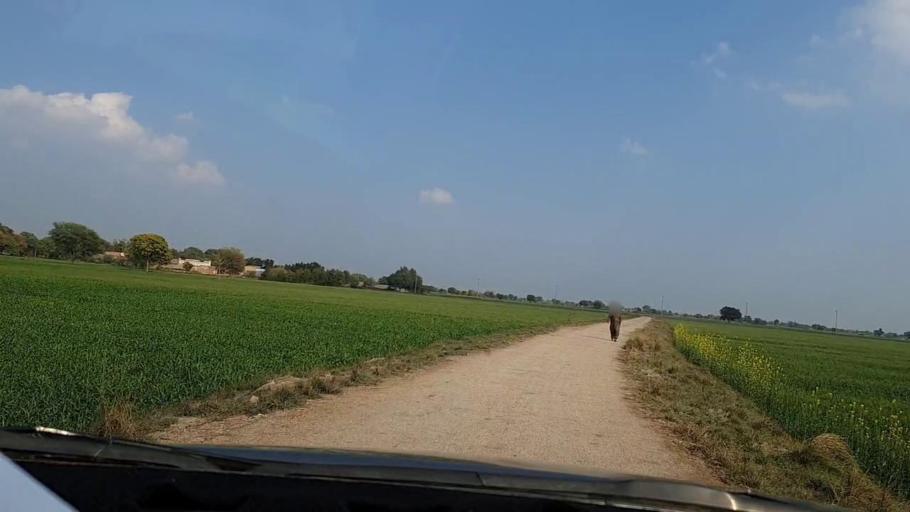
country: PK
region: Sindh
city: Sakrand
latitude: 26.1675
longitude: 68.3611
